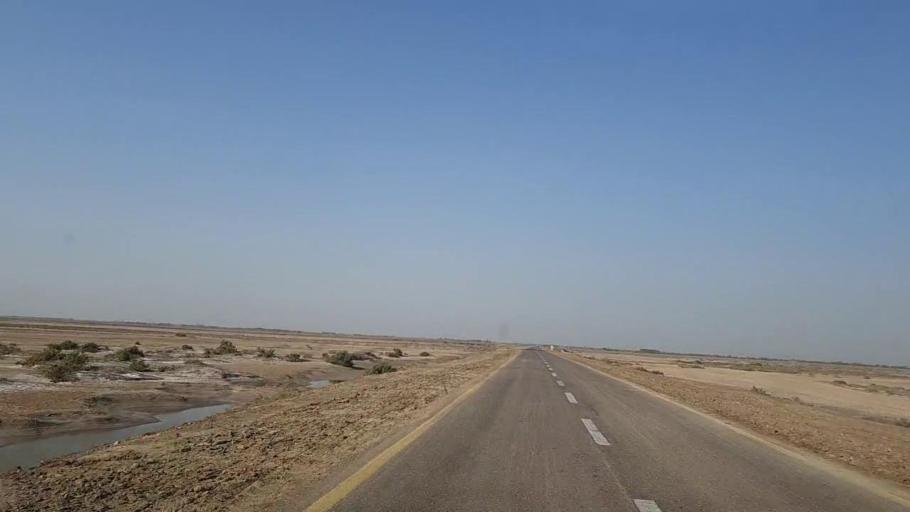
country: PK
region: Sindh
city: Jati
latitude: 24.4930
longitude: 68.3757
